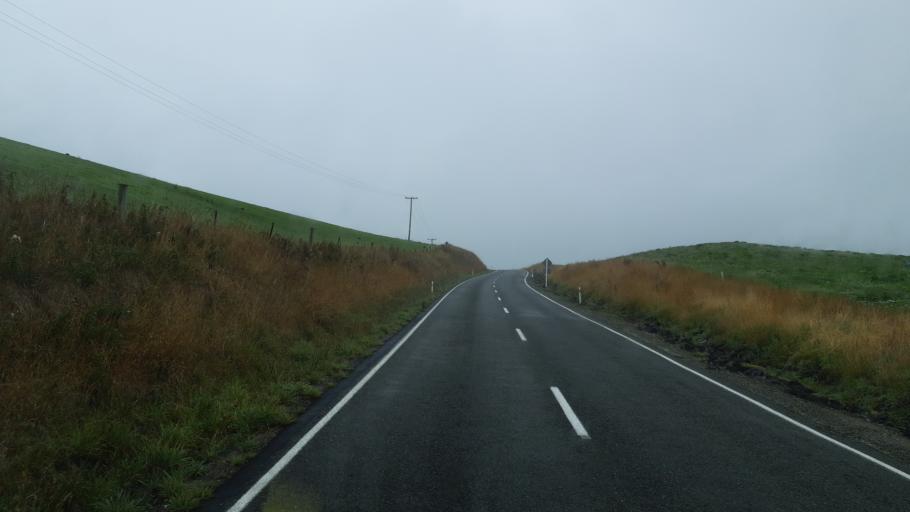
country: NZ
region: Otago
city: Oamaru
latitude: -44.9125
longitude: 170.8358
